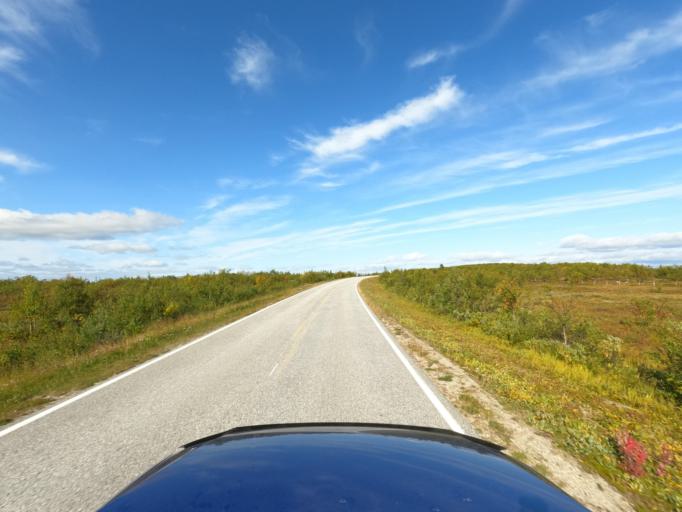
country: NO
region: Finnmark Fylke
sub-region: Karasjok
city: Karasjohka
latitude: 69.7099
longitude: 25.2431
